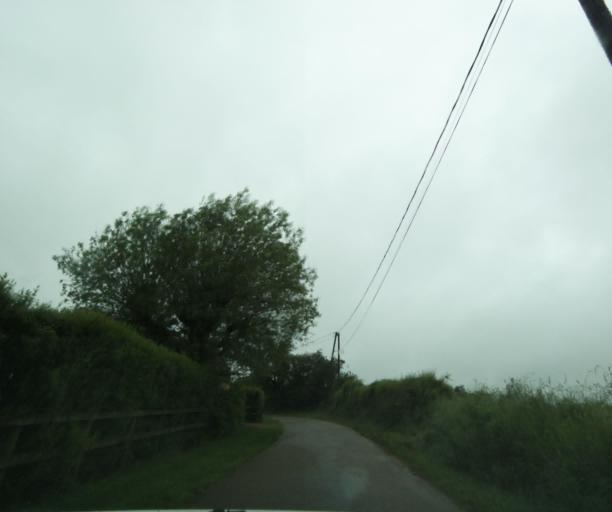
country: FR
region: Bourgogne
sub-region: Departement de Saone-et-Loire
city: Charolles
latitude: 46.4104
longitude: 4.3235
